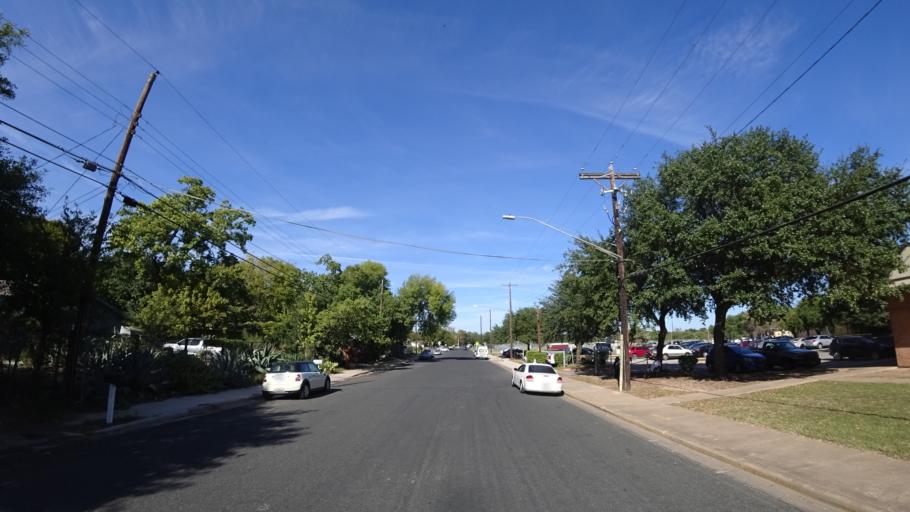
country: US
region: Texas
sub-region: Travis County
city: Austin
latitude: 30.2587
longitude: -97.6825
